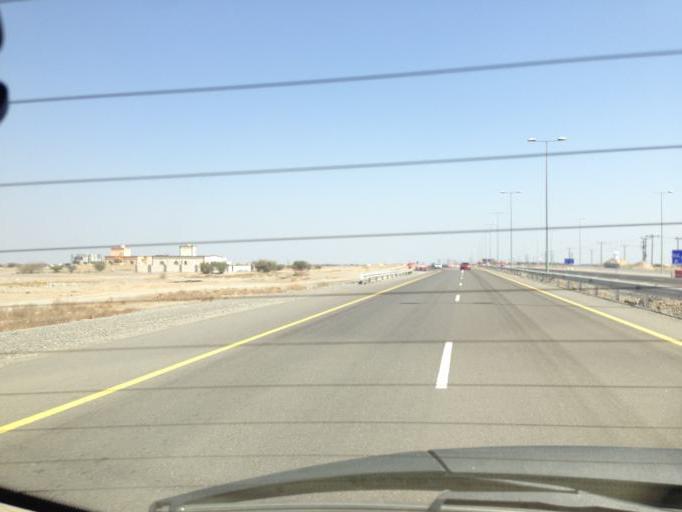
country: OM
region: Al Batinah
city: Rustaq
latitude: 23.5826
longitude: 57.4950
